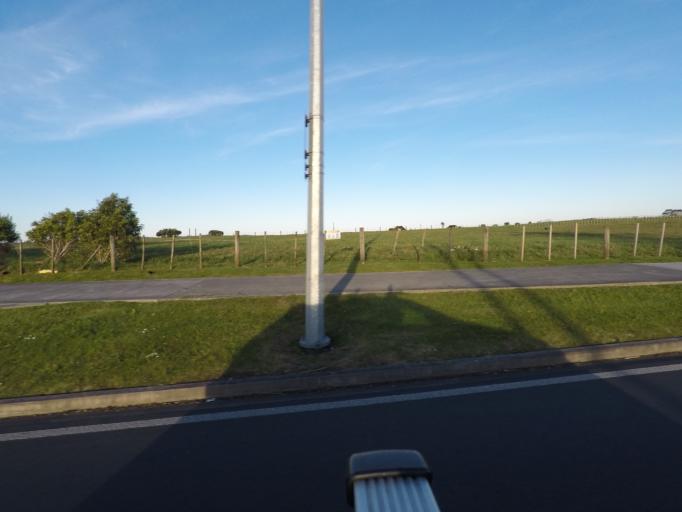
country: NZ
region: Auckland
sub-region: Auckland
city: Rosebank
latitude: -36.8545
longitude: 174.6513
